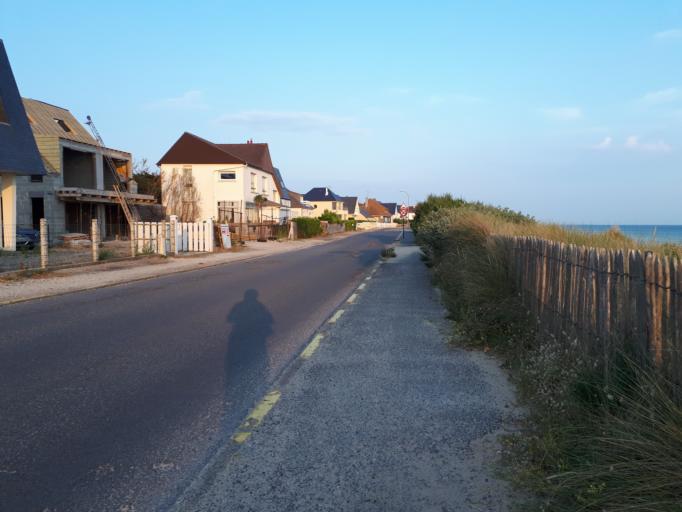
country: FR
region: Lower Normandy
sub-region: Departement de la Manche
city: Barneville-Plage
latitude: 49.3641
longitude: -1.7656
